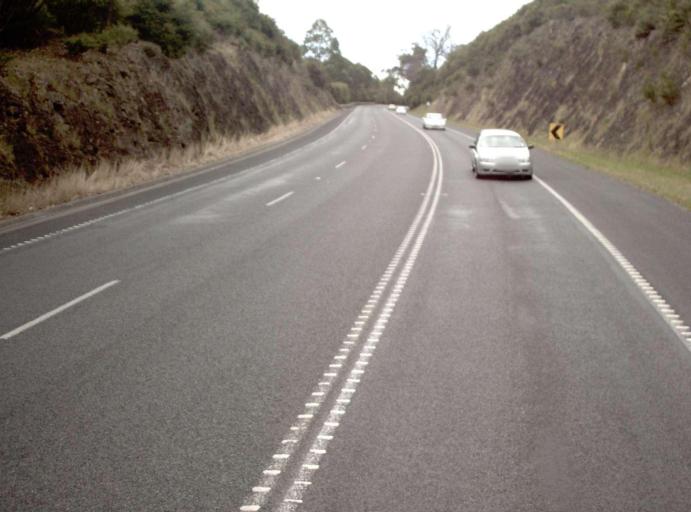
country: AU
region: Victoria
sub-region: Yarra Ranges
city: Badger Creek
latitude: -37.6791
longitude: 145.4885
